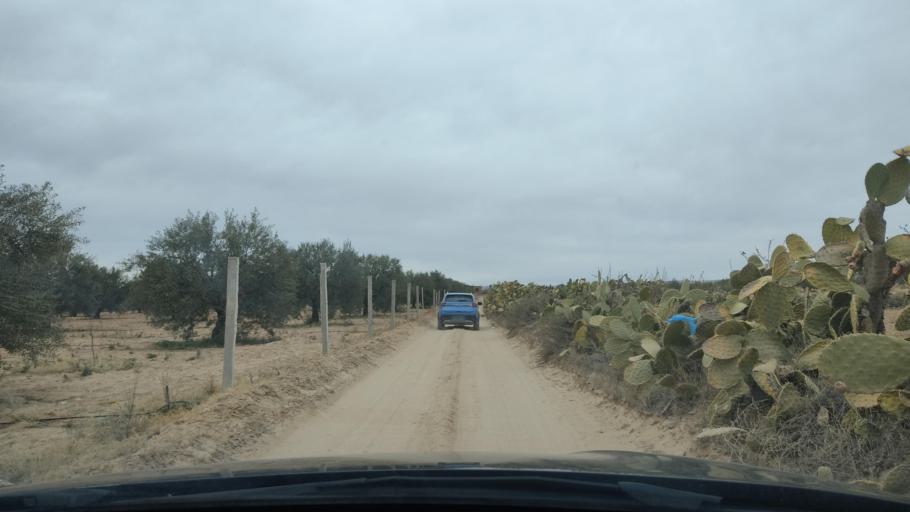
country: TN
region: Al Qasrayn
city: Kasserine
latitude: 35.2278
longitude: 8.9150
